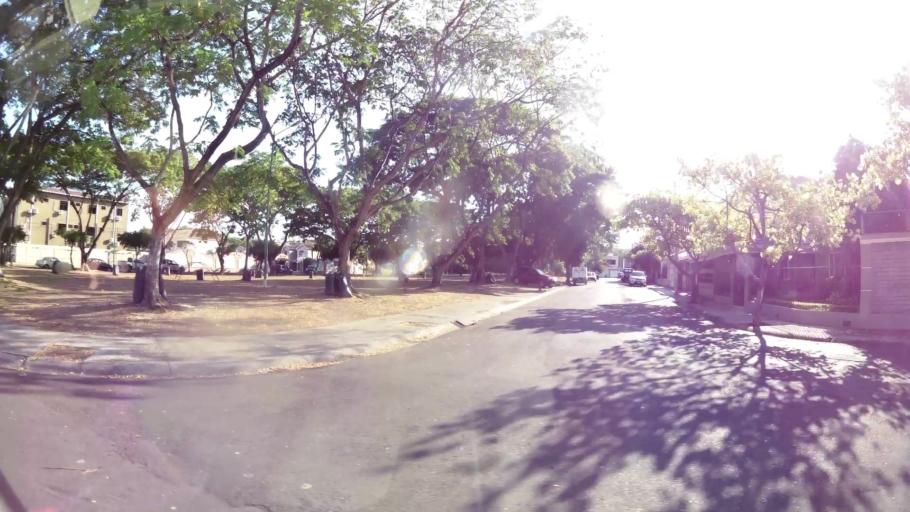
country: EC
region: Guayas
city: Santa Lucia
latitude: -2.1920
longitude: -79.9717
